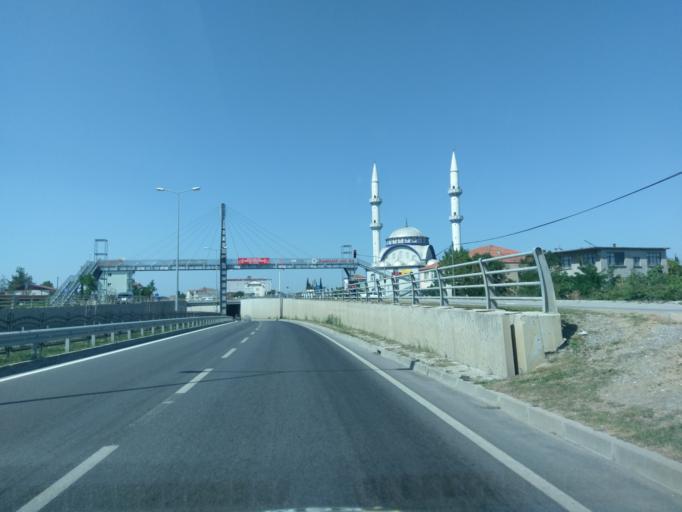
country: TR
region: Samsun
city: Bafra
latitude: 41.5503
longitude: 35.9262
